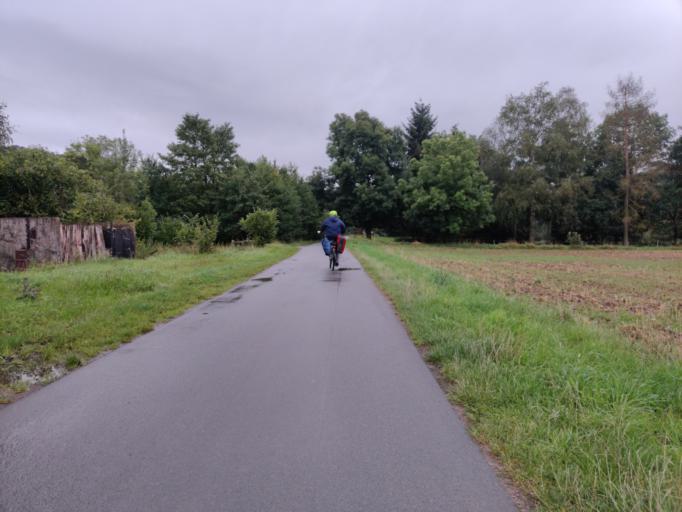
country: DE
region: Lower Saxony
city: Furstenberg
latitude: 51.7101
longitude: 9.3915
